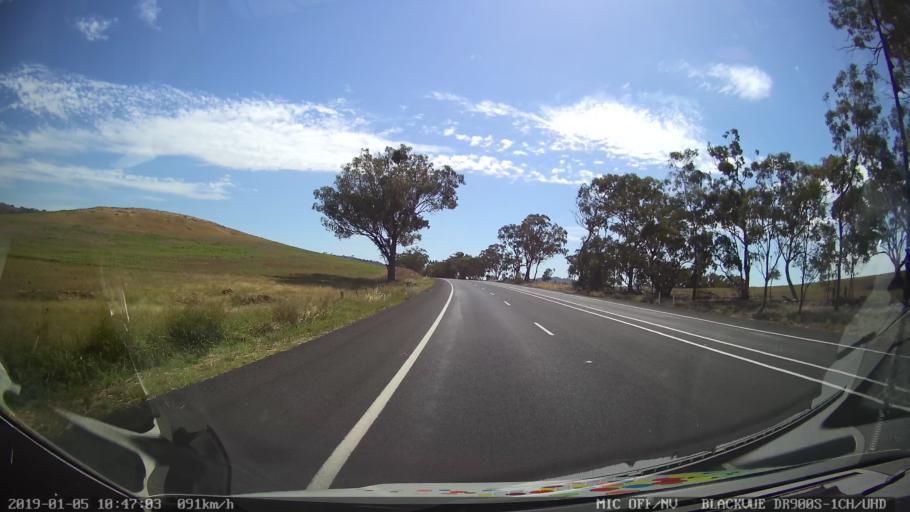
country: AU
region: New South Wales
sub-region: Warrumbungle Shire
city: Coonabarabran
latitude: -31.4479
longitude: 149.0278
